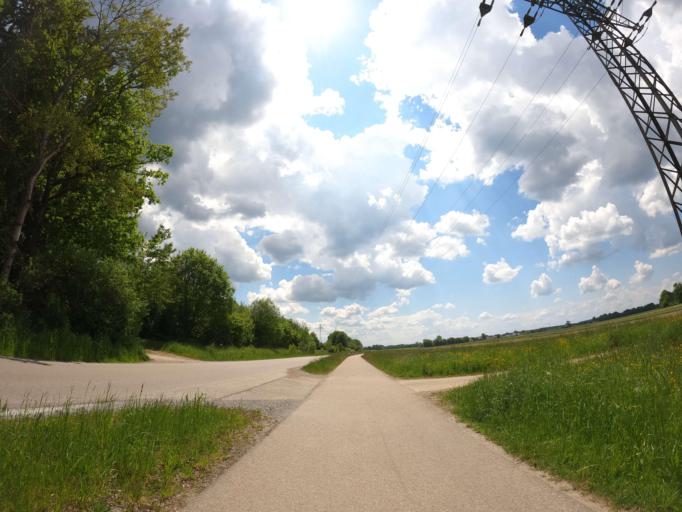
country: DE
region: Bavaria
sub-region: Upper Bavaria
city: Sauerlach
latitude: 47.9889
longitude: 11.6589
